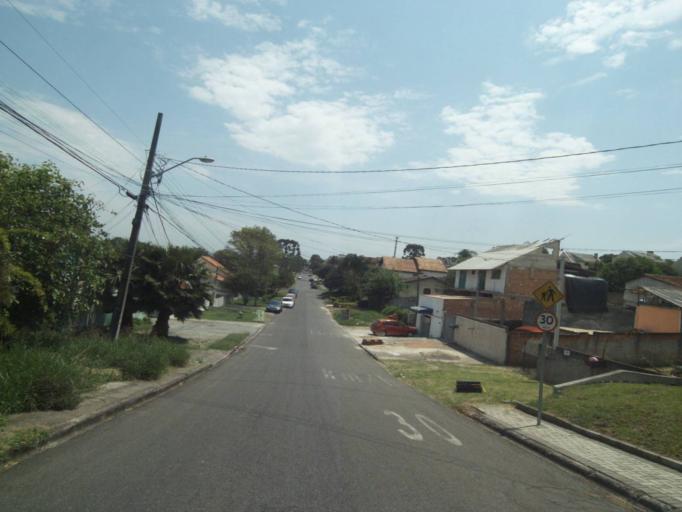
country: BR
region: Parana
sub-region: Pinhais
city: Pinhais
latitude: -25.4235
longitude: -49.2076
